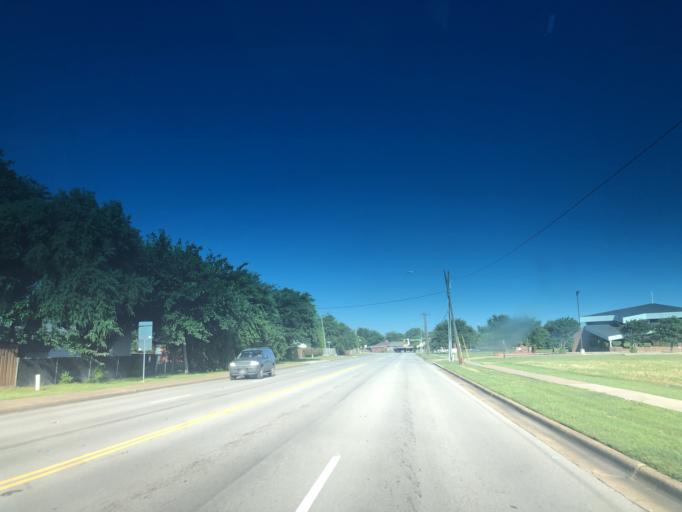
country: US
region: Texas
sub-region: Dallas County
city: Grand Prairie
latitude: 32.6989
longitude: -96.9998
